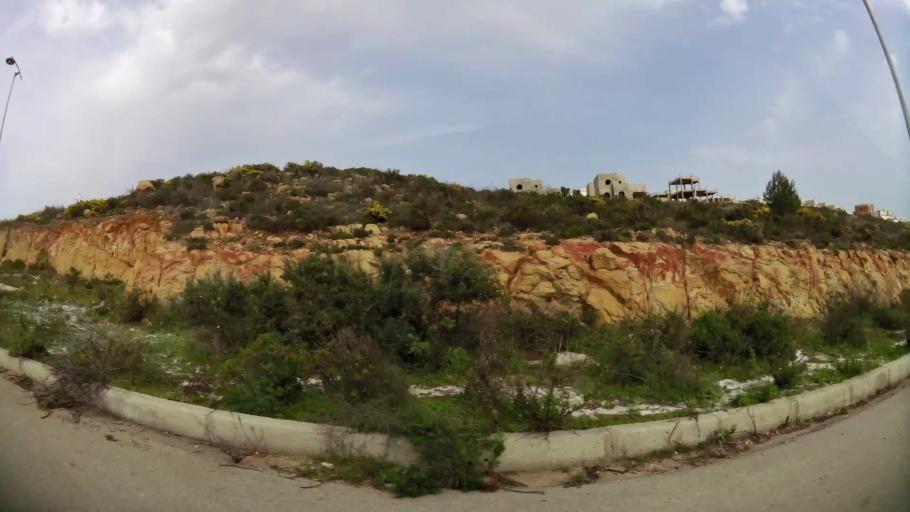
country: MA
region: Tanger-Tetouan
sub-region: Tanger-Assilah
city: Boukhalef
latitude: 35.6987
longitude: -5.9417
